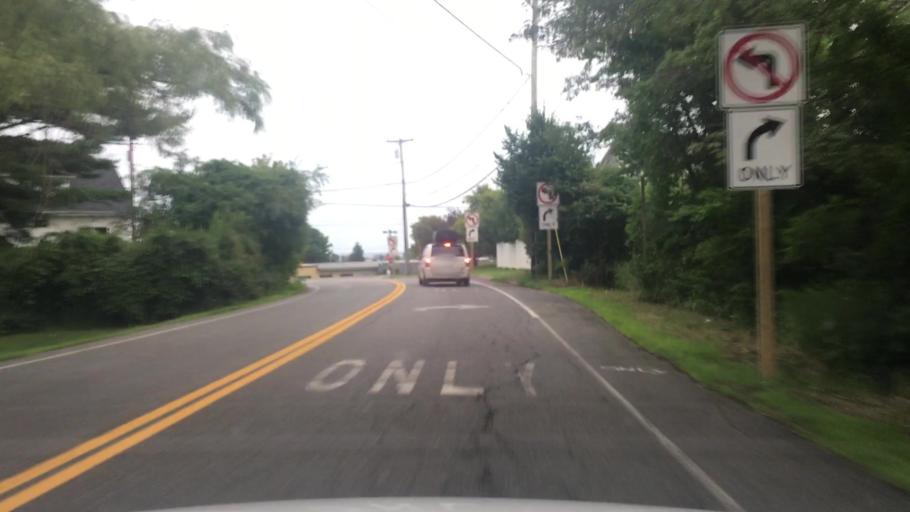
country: US
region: Maine
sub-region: York County
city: Wells Beach Station
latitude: 43.3106
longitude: -70.5857
